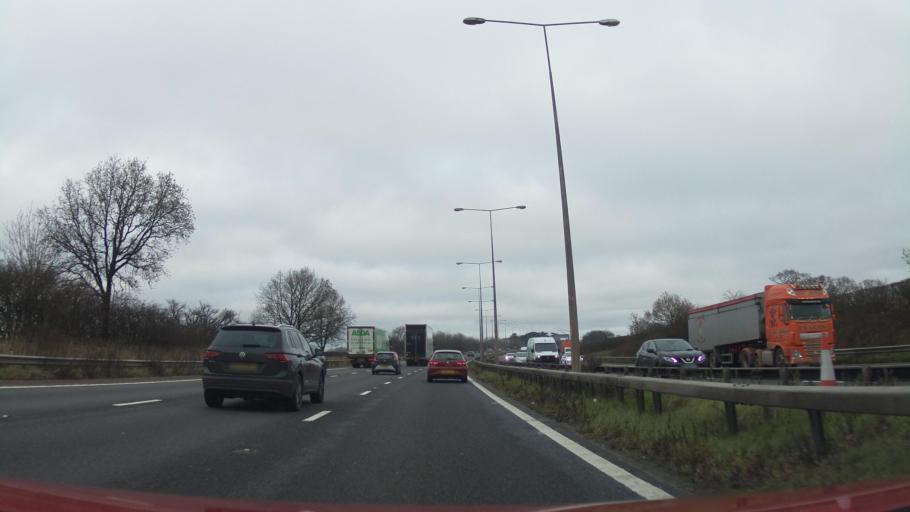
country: GB
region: England
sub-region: Lancashire
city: Clayton-le-Woods
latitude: 53.7067
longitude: -2.6743
